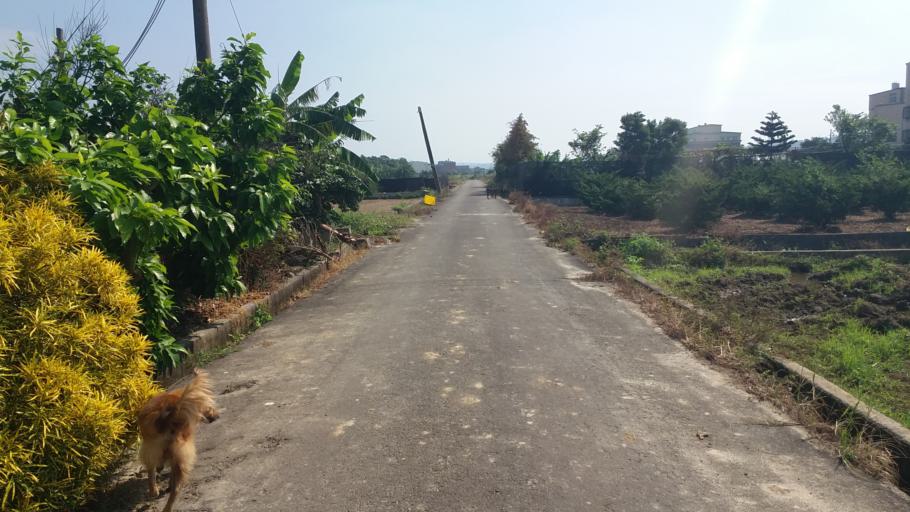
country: TW
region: Taiwan
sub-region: Hsinchu
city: Zhubei
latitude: 24.8975
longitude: 121.0147
